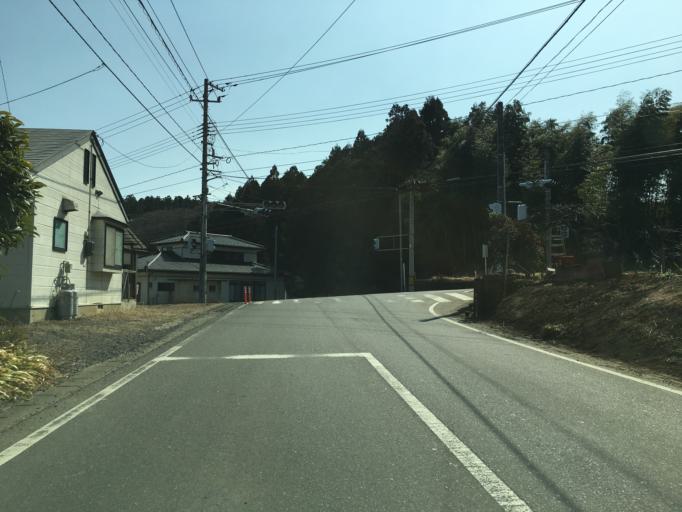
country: JP
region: Fukushima
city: Ishikawa
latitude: 37.1429
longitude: 140.4011
